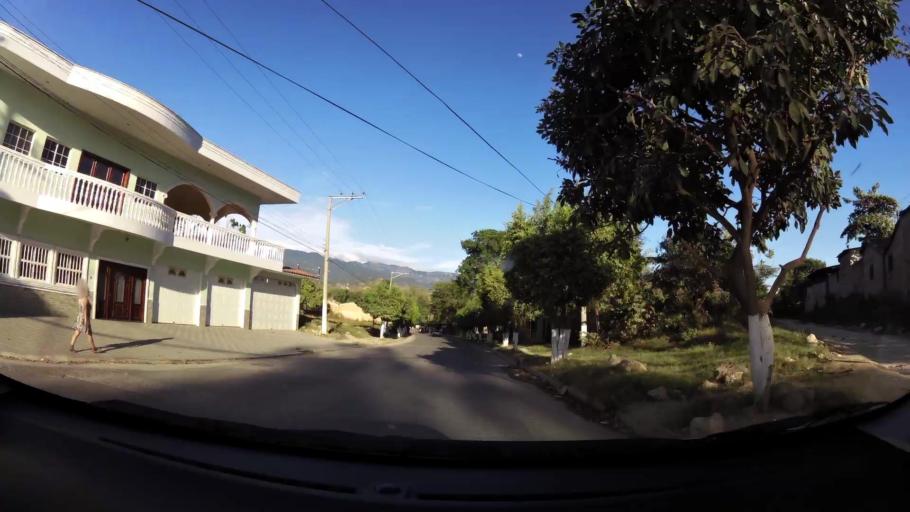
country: SV
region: Santa Ana
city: Metapan
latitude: 14.3295
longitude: -89.4519
